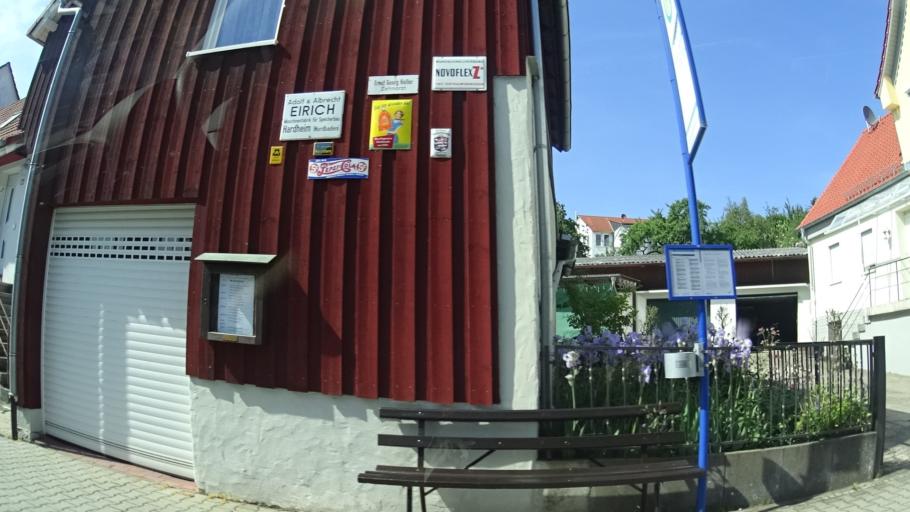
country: DE
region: Bavaria
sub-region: Regierungsbezirk Unterfranken
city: Rudenau
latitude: 49.7116
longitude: 9.0998
